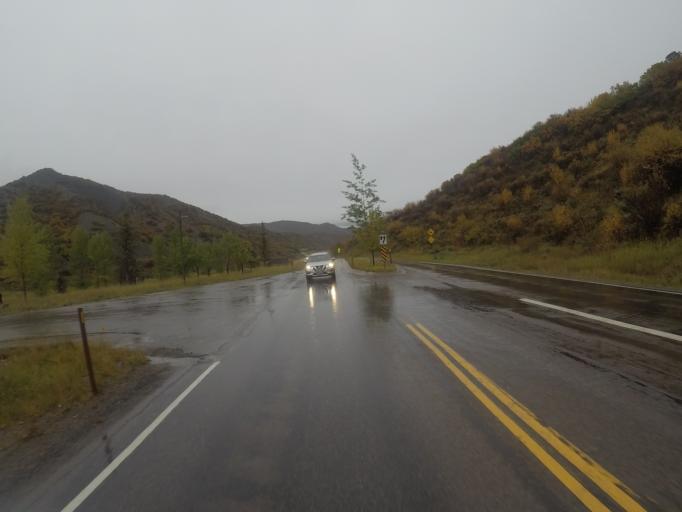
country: US
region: Colorado
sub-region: Pitkin County
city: Snowmass Village
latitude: 39.2267
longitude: -106.9192
